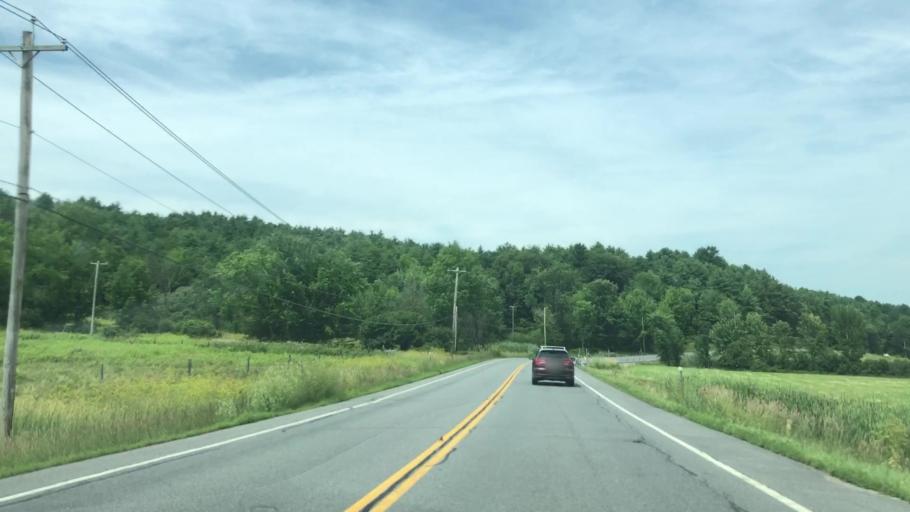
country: US
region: New York
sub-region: Washington County
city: Whitehall
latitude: 43.4926
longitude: -73.4286
